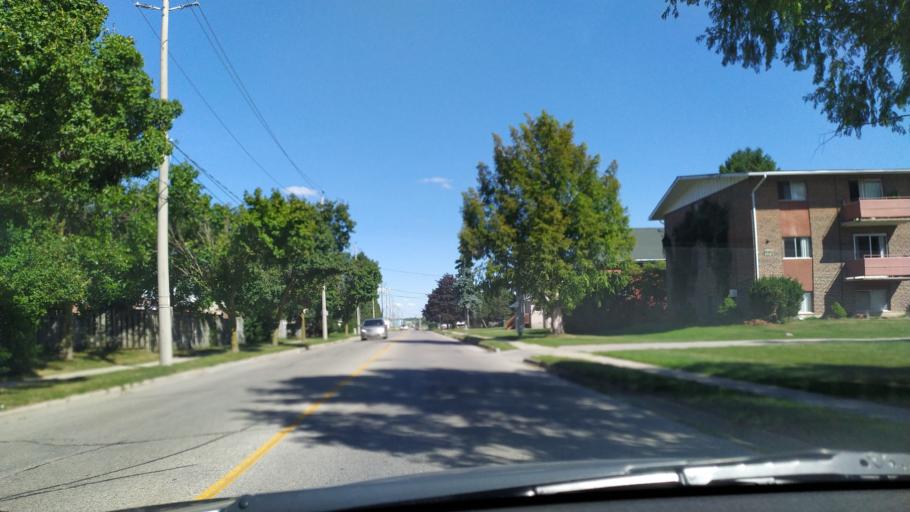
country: CA
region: Ontario
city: Stratford
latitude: 43.3603
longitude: -80.9686
